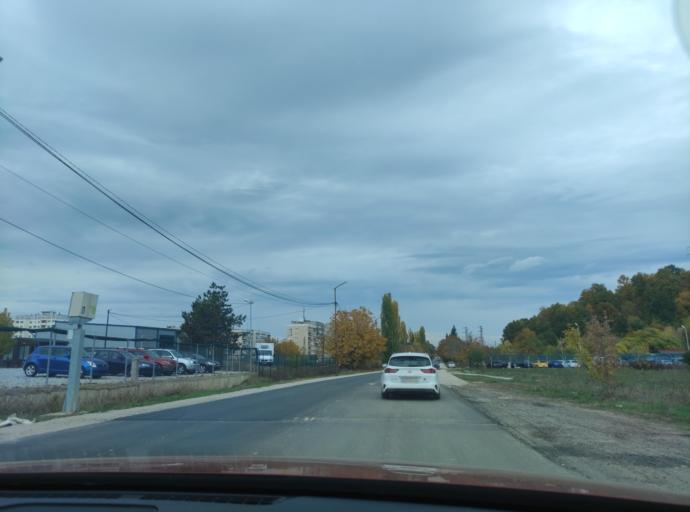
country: BG
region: Montana
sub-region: Obshtina Montana
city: Montana
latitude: 43.3954
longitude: 23.2404
